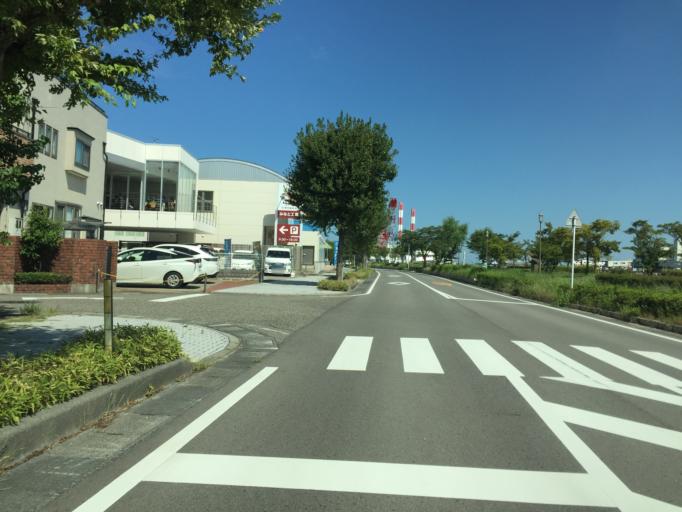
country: JP
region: Niigata
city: Niigata-shi
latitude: 37.9268
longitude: 139.0568
